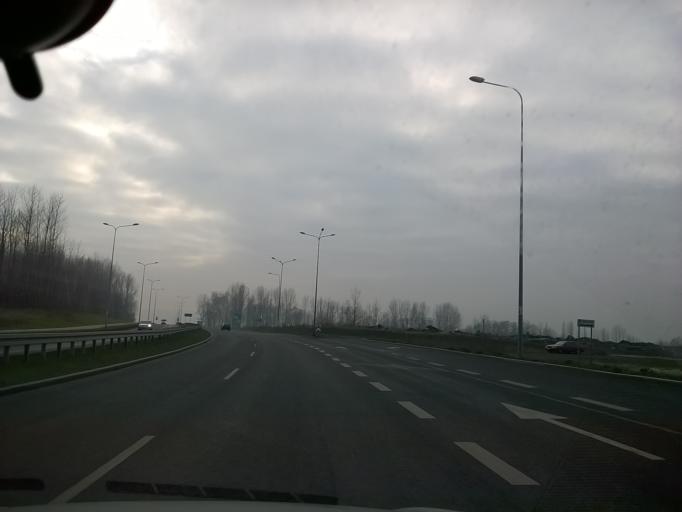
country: PL
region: Silesian Voivodeship
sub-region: Ruda Slaska
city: Ruda Slaska
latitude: 50.2904
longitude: 18.8518
